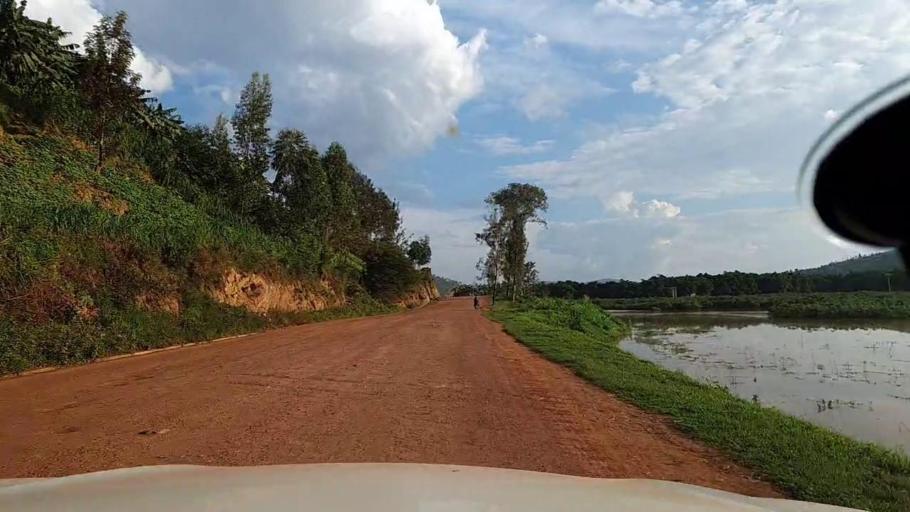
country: RW
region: Kigali
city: Kigali
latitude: -1.9361
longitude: 29.9979
